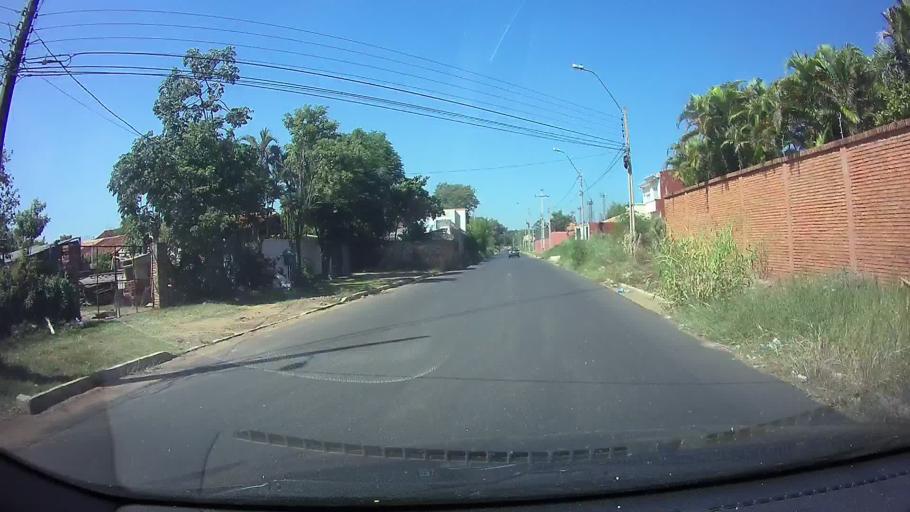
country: PY
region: Central
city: Fernando de la Mora
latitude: -25.2843
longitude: -57.5461
